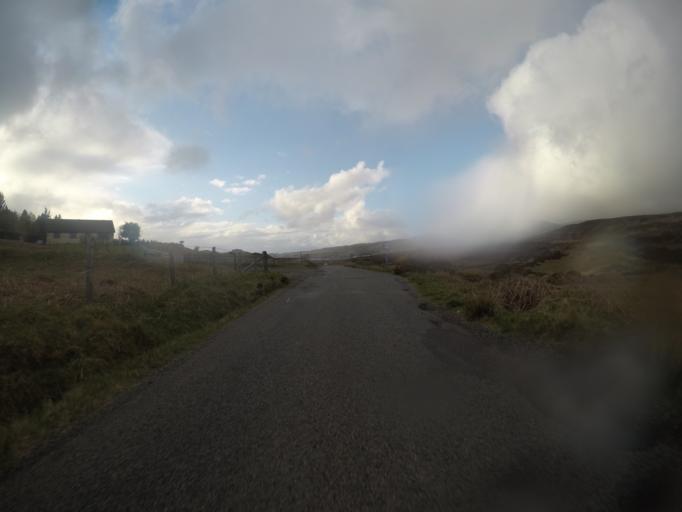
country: GB
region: Scotland
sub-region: Highland
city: Isle of Skye
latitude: 57.4658
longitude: -6.2978
